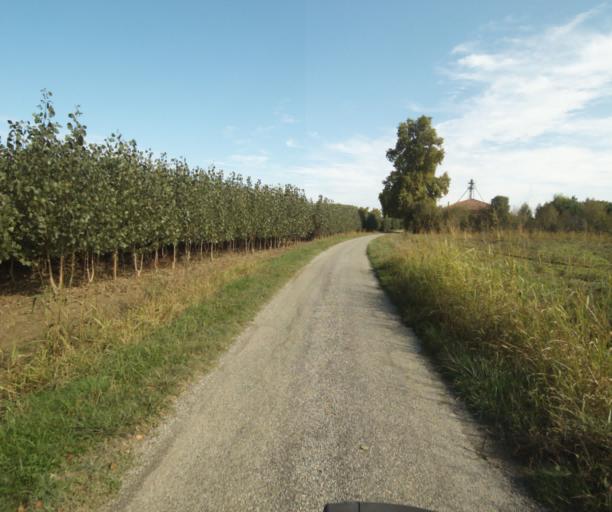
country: FR
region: Midi-Pyrenees
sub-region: Departement du Tarn-et-Garonne
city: Finhan
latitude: 43.8984
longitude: 1.2125
